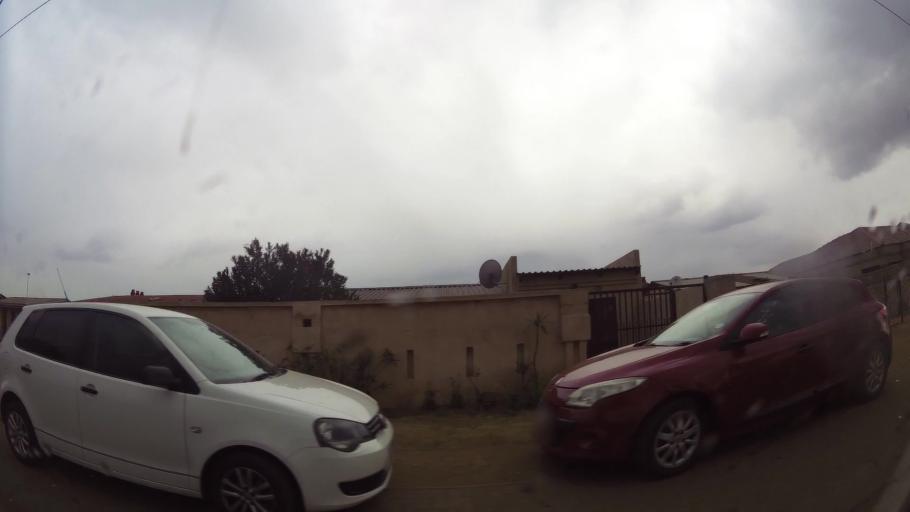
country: ZA
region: Gauteng
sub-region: Ekurhuleni Metropolitan Municipality
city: Germiston
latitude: -26.3411
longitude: 28.1440
